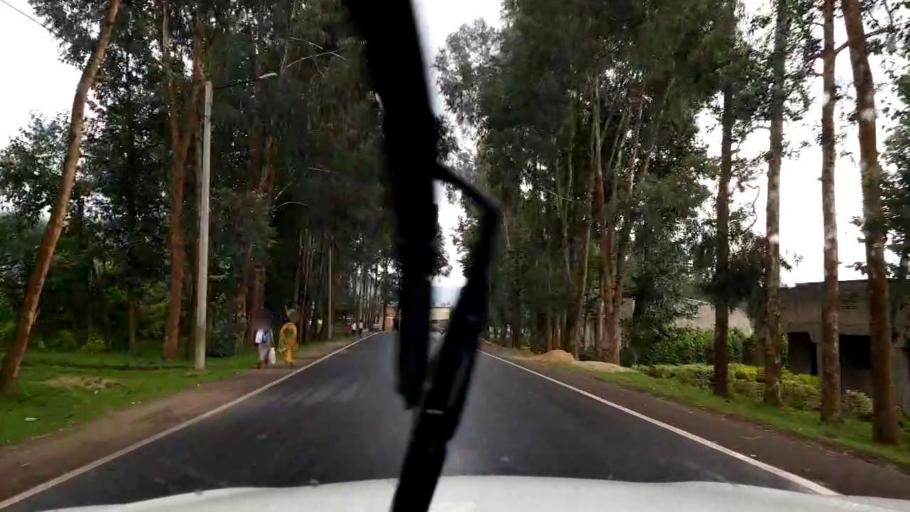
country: RW
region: Western Province
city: Gisenyi
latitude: -1.6761
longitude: 29.3557
